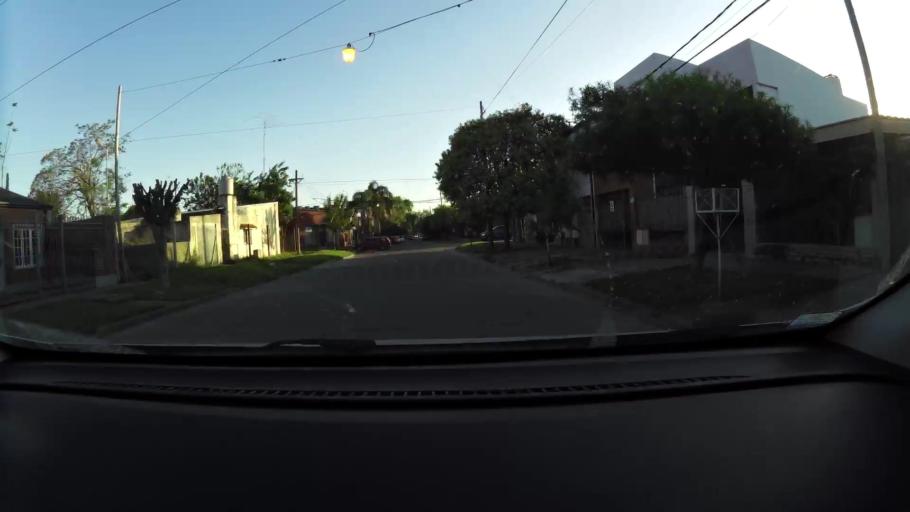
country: AR
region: Santa Fe
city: Santa Fe de la Vera Cruz
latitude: -31.5979
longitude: -60.6873
